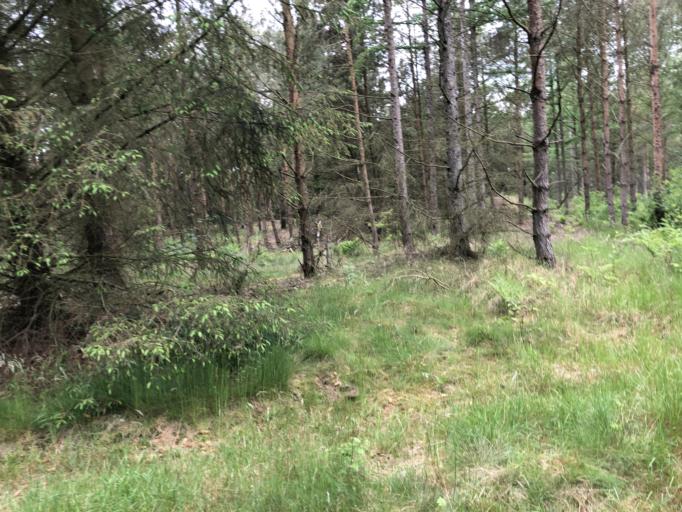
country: DK
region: Central Jutland
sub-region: Holstebro Kommune
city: Ulfborg
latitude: 56.2770
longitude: 8.3656
